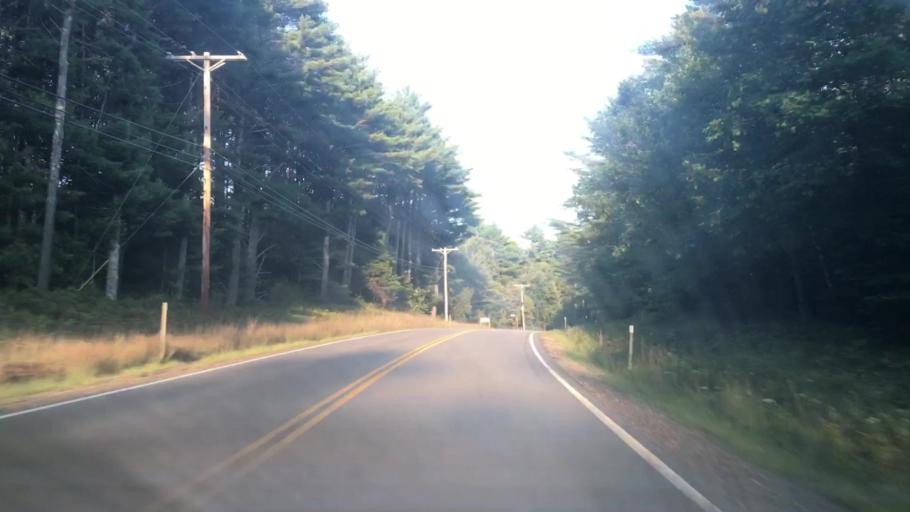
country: US
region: New Hampshire
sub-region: Belknap County
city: Gilmanton
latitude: 43.4289
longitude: -71.3460
